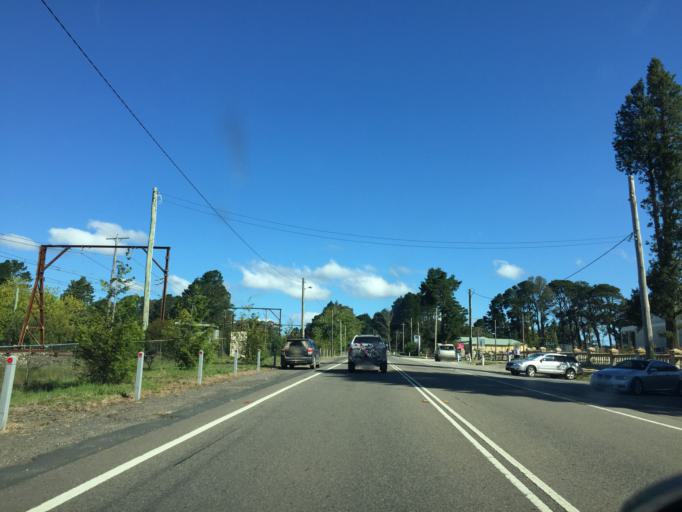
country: AU
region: New South Wales
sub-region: Blue Mountains Municipality
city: Blackheath
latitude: -33.6762
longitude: 150.2816
